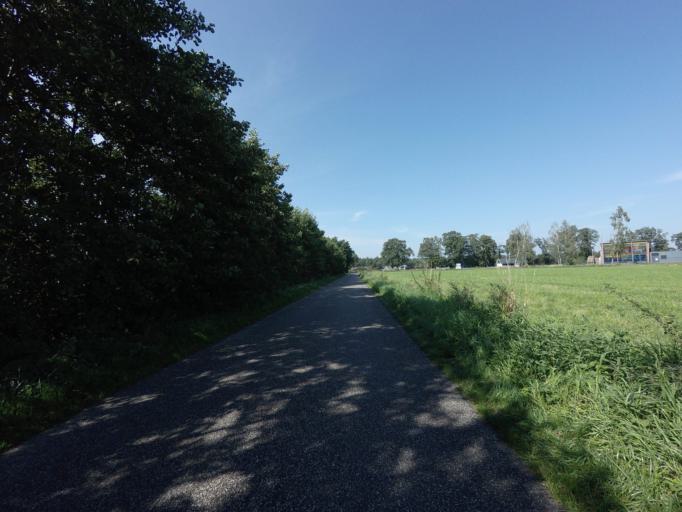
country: NL
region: Overijssel
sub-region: Gemeente Haaksbergen
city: Haaksbergen
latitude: 52.2126
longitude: 6.7548
